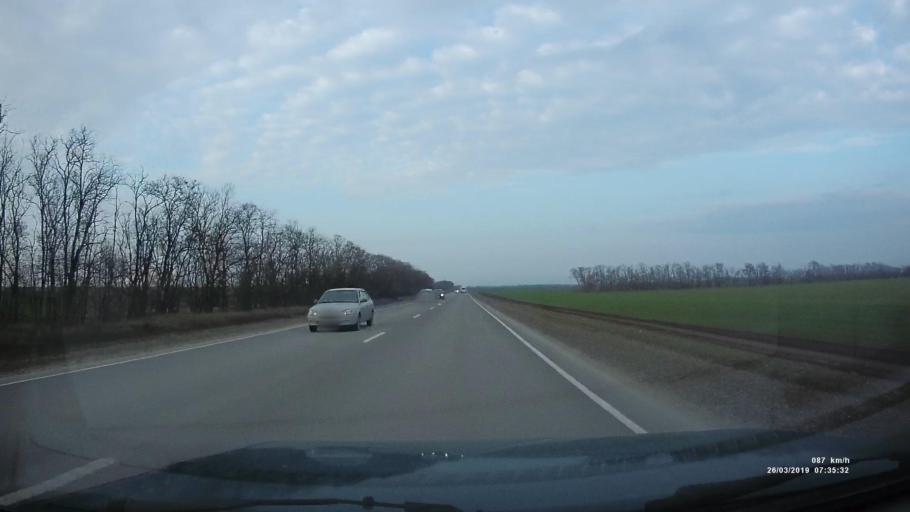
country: RU
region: Rostov
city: Novobessergenovka
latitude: 47.2075
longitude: 38.7367
